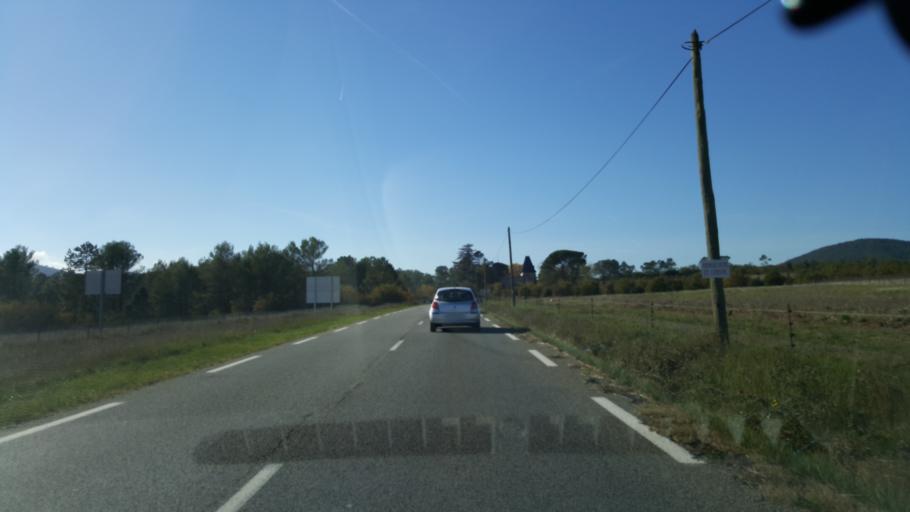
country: FR
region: Provence-Alpes-Cote d'Azur
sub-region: Departement du Var
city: Nans-les-Pins
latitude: 43.3917
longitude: 5.7864
